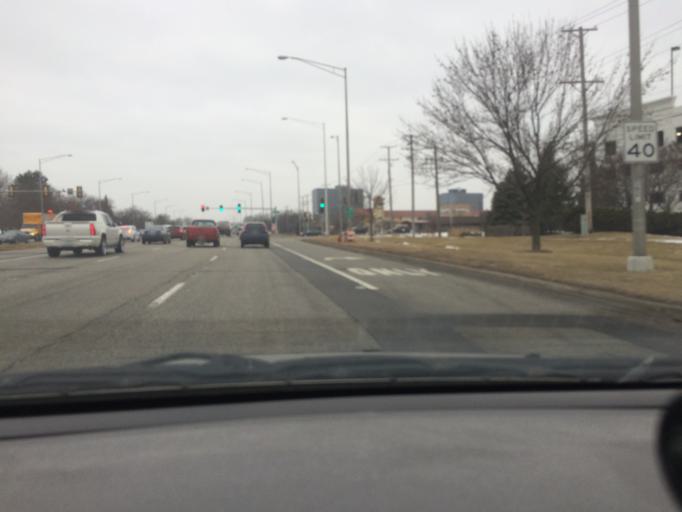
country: US
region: Illinois
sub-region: Cook County
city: Hoffman Estates
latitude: 42.0377
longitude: -88.0344
